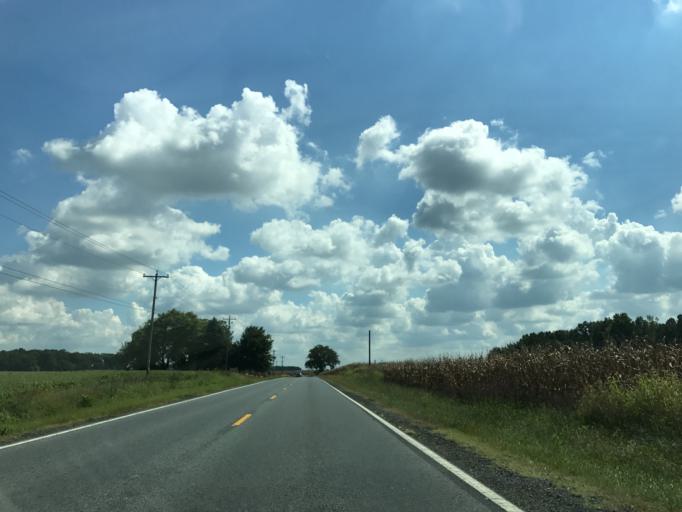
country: US
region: Maryland
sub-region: Queen Anne's County
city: Centreville
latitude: 39.0055
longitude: -75.9781
